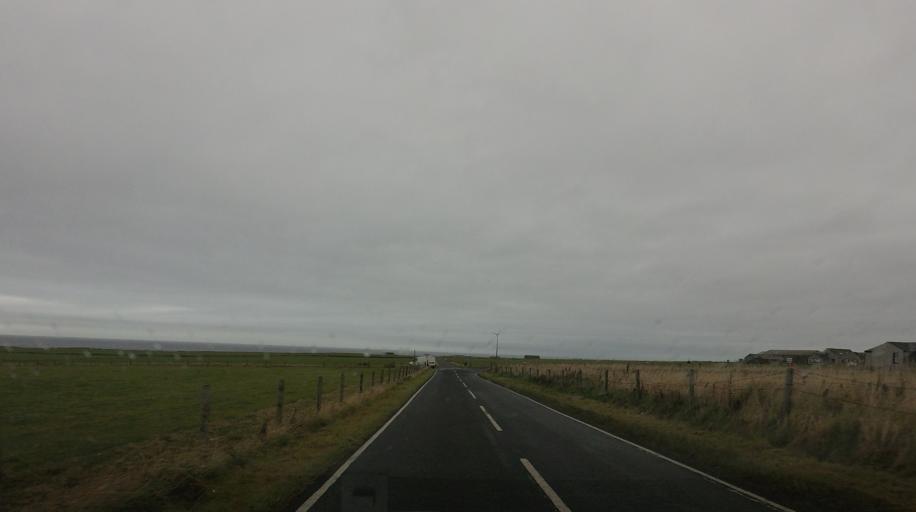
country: GB
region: Scotland
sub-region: Orkney Islands
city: Stromness
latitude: 59.1309
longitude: -3.3035
